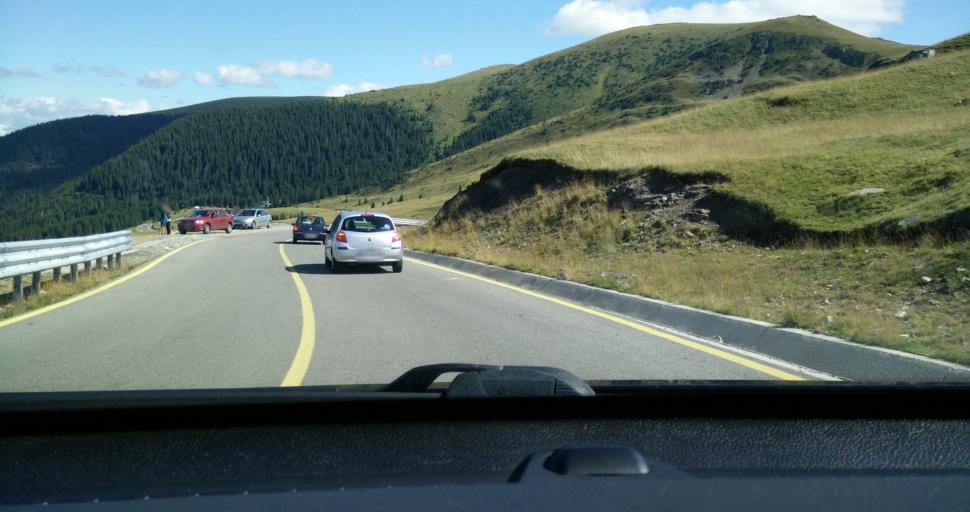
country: RO
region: Gorj
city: Novaci-Straini
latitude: 45.3816
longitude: 23.6418
